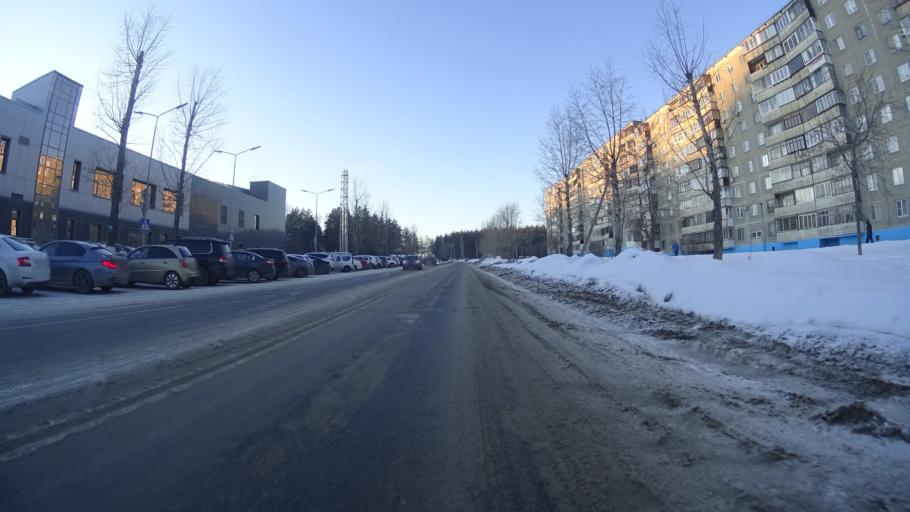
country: RU
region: Chelyabinsk
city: Roshchino
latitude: 55.1952
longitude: 61.2996
